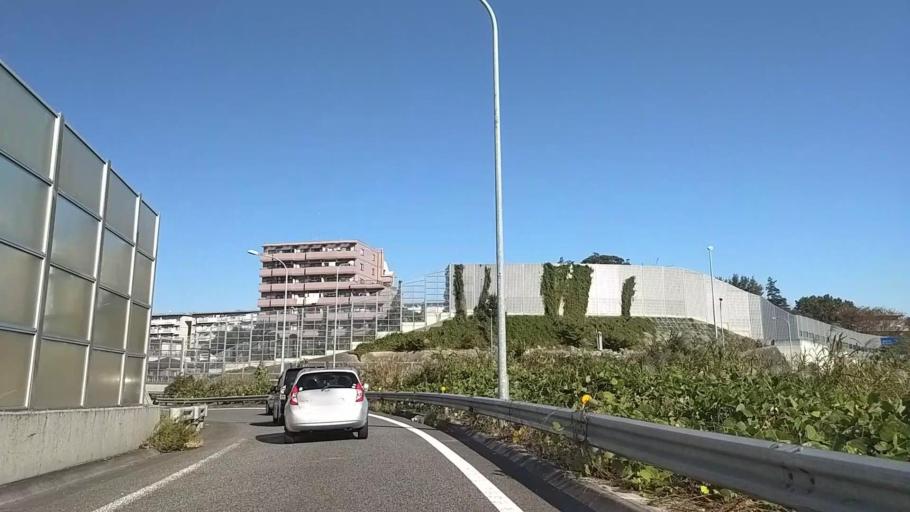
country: JP
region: Kanagawa
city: Yokohama
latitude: 35.4525
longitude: 139.5604
